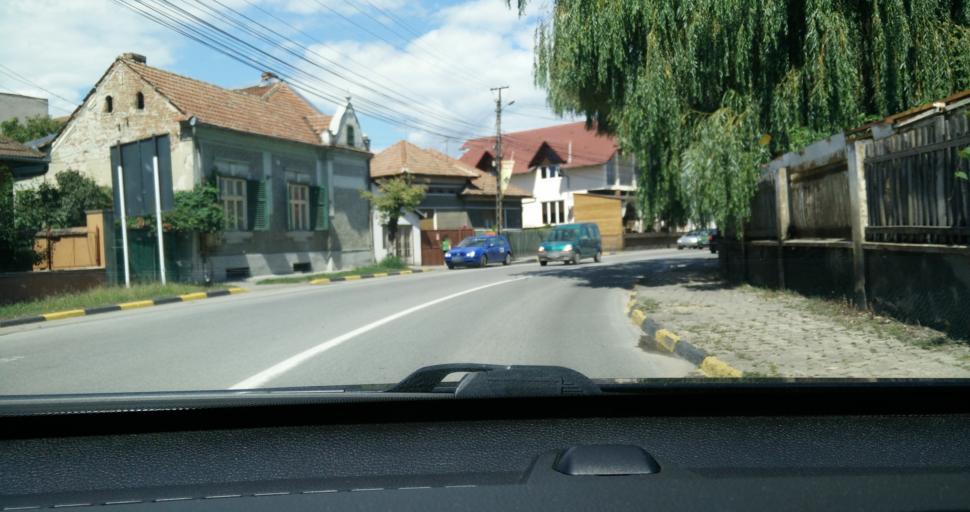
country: RO
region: Alba
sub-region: Municipiul Sebes
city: Sebes
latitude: 45.9562
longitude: 23.5652
